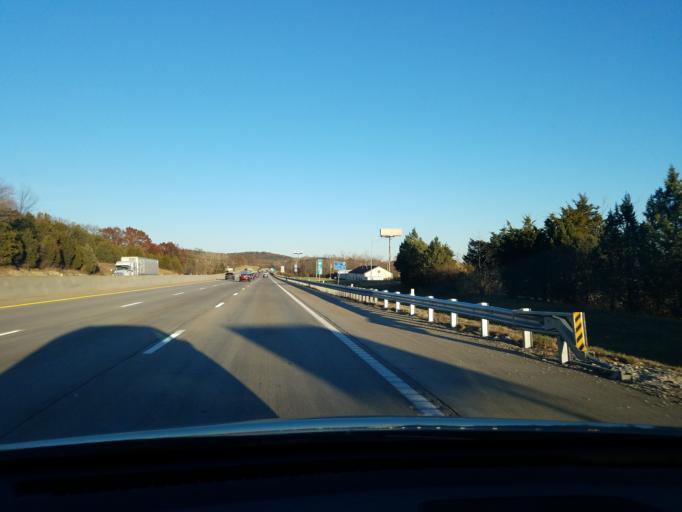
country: US
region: Missouri
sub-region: Franklin County
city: Gray Summit
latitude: 38.4853
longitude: -90.8147
